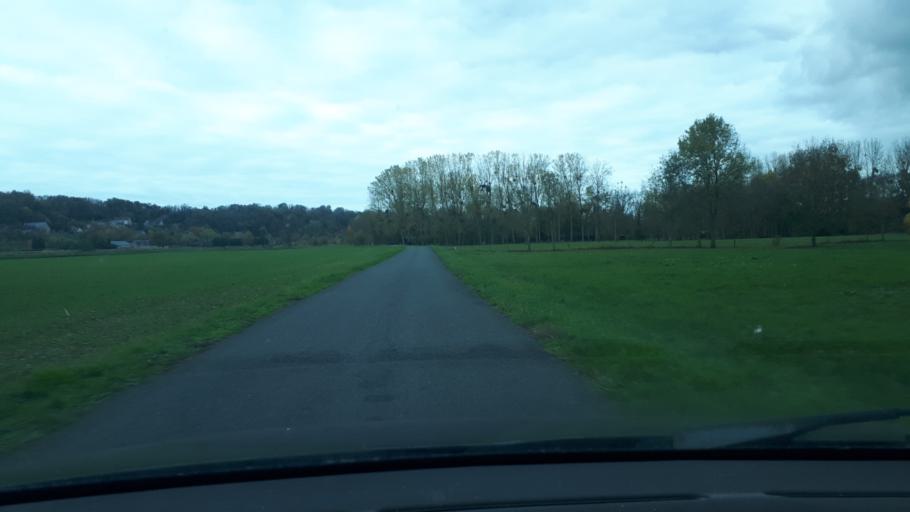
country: FR
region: Centre
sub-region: Departement du Loir-et-Cher
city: Lunay
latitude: 47.7690
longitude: 0.9372
